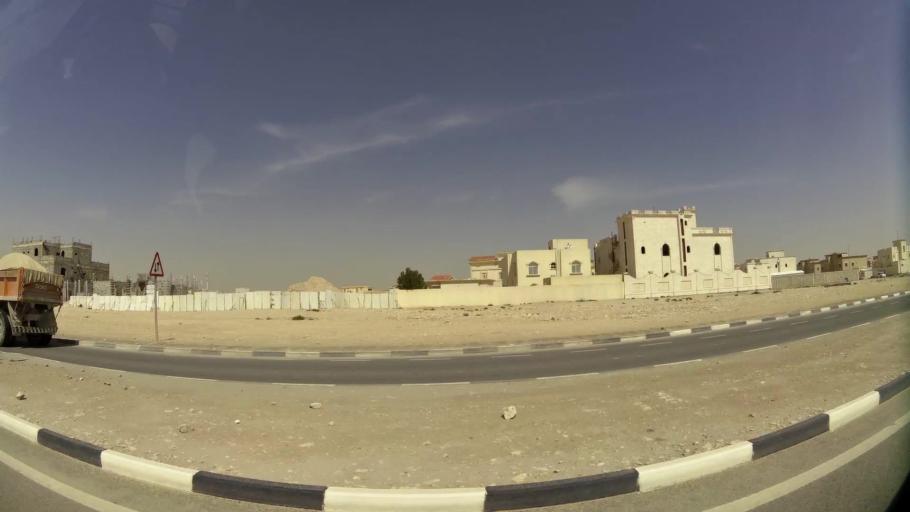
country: QA
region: Baladiyat ar Rayyan
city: Ar Rayyan
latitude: 25.2490
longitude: 51.3871
